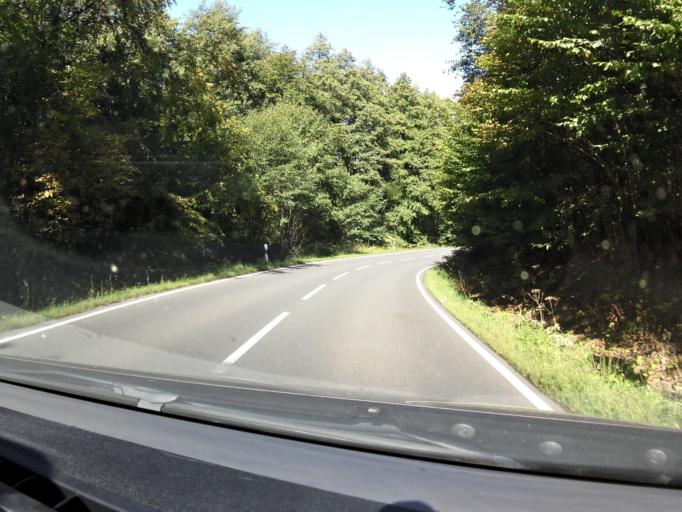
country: DE
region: Saxony-Anhalt
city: Gernrode
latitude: 51.6966
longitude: 11.1321
